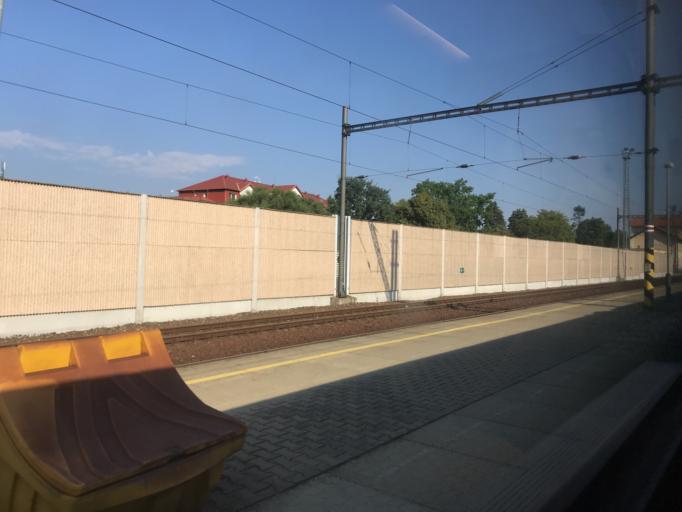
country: CZ
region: Jihocesky
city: Plana nad Luznici
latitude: 49.3513
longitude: 14.7073
